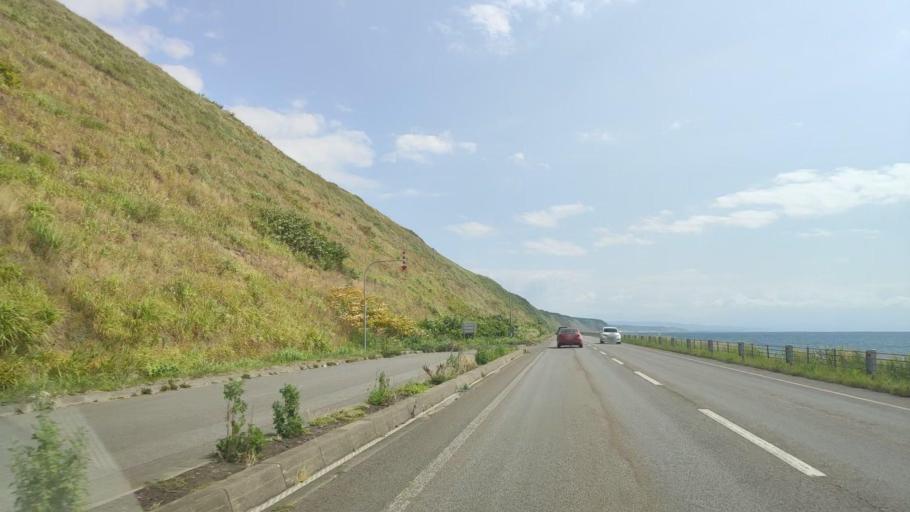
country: JP
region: Hokkaido
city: Rumoi
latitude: 44.0677
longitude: 141.6629
